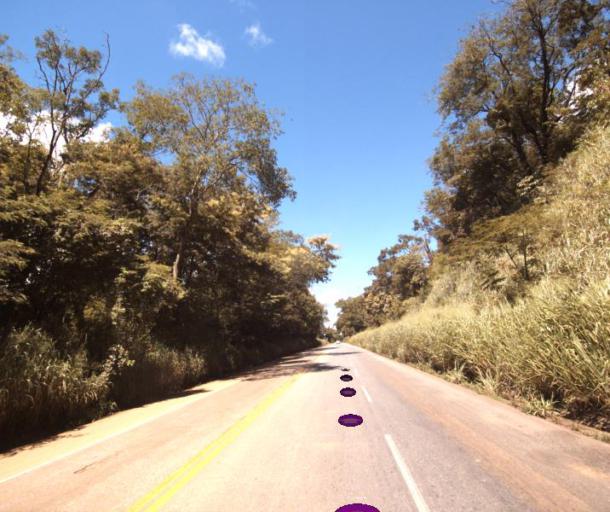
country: BR
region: Goias
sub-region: Anapolis
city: Anapolis
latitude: -16.1048
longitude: -49.0305
